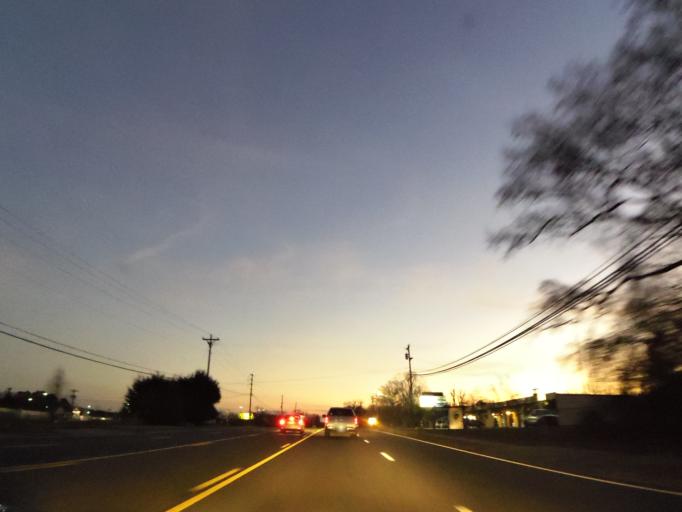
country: US
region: Georgia
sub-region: Whitfield County
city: Dalton
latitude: 34.8239
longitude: -84.9450
